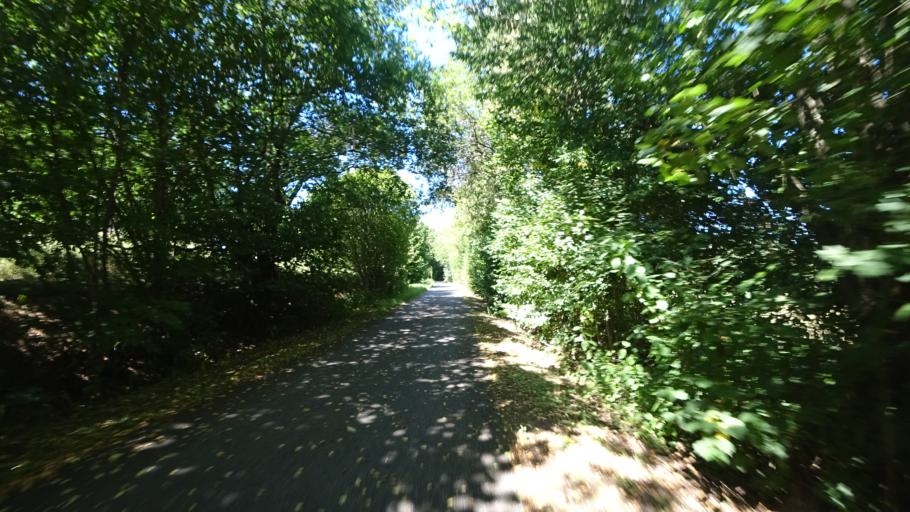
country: DE
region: Rheinland-Pfalz
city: Neuerkirch
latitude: 50.0189
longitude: 7.4836
